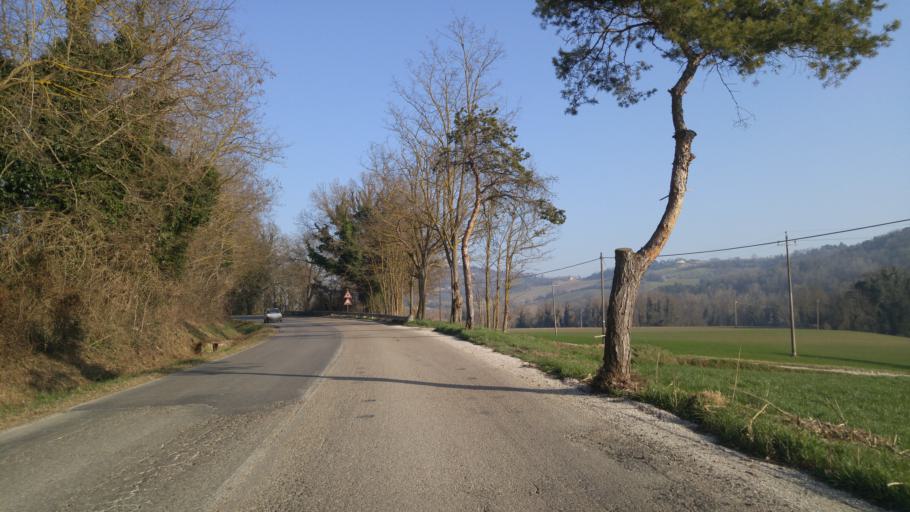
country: IT
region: The Marches
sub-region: Provincia di Pesaro e Urbino
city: Fenile
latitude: 43.8331
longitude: 12.9206
